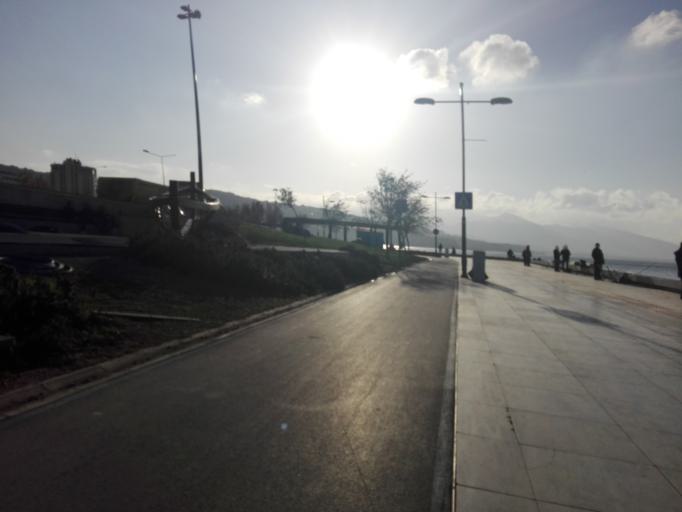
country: TR
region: Izmir
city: Izmir
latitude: 38.4174
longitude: 27.1236
